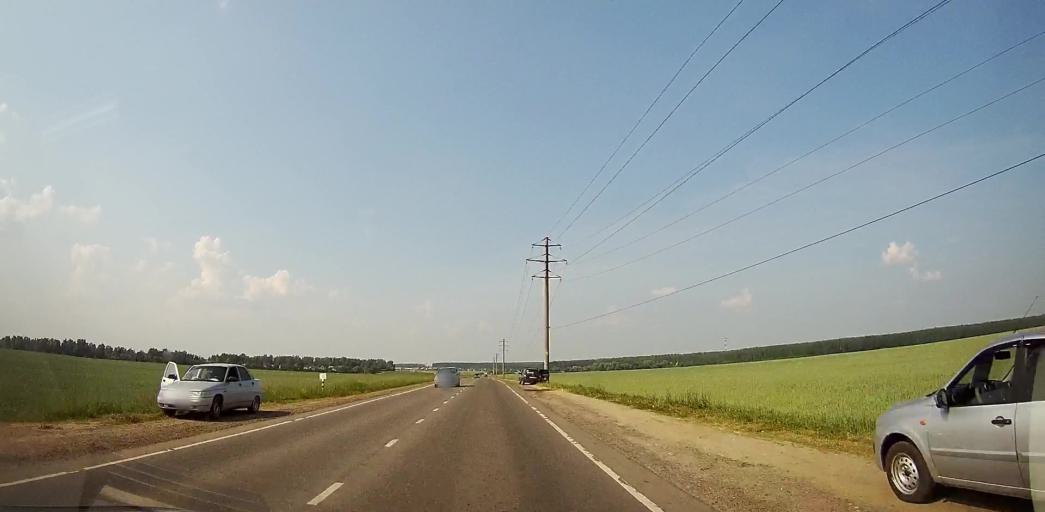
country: RU
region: Moskovskaya
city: Barybino
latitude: 55.2545
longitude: 37.9187
